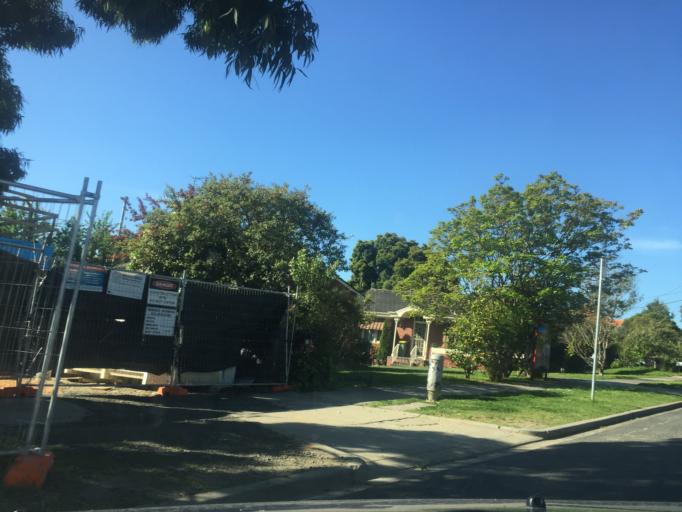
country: AU
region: Victoria
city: Ivanhoe East
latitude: -37.7751
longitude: 145.0549
